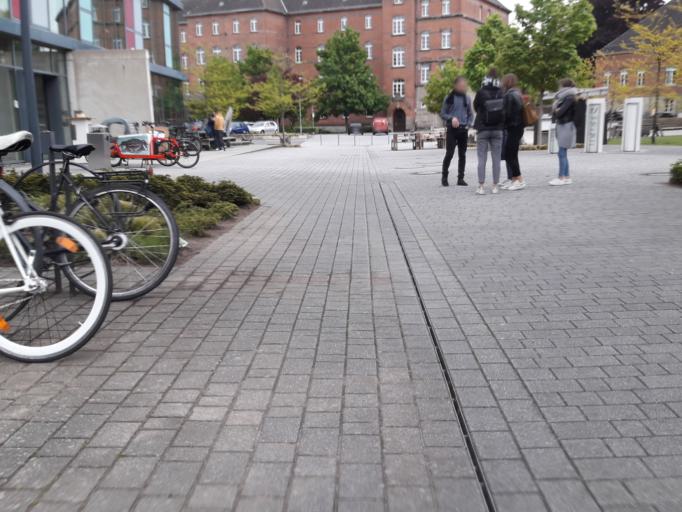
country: DE
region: North Rhine-Westphalia
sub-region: Regierungsbezirk Detmold
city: Detmold
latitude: 51.9366
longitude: 8.8657
